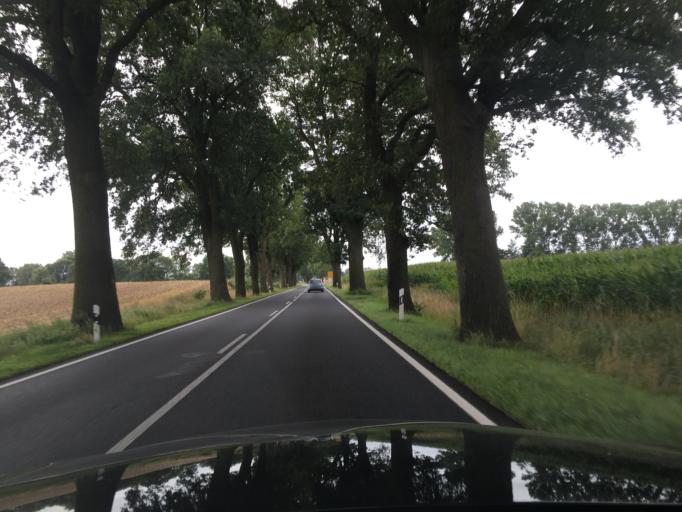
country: DE
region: Brandenburg
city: Gransee
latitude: 52.9412
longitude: 13.1532
